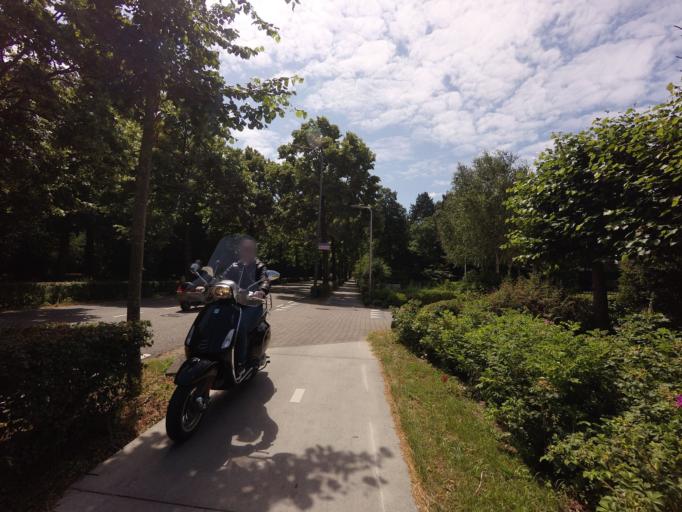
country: NL
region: South Holland
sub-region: Gemeente Teylingen
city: Sassenheim
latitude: 52.2060
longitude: 4.5098
